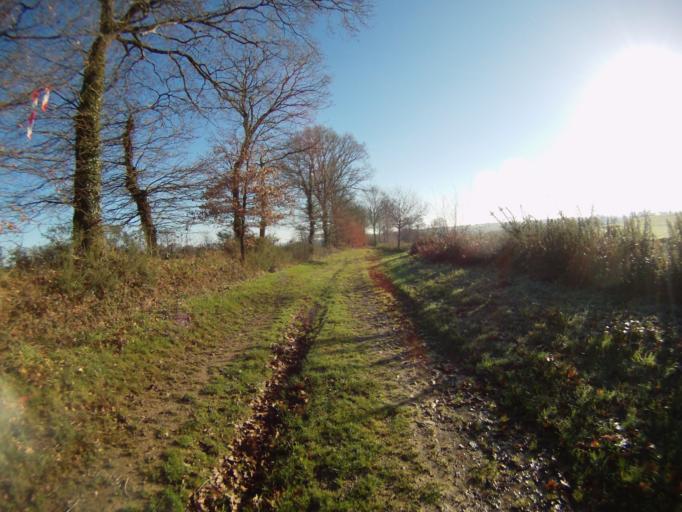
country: FR
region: Brittany
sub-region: Departement d'Ille-et-Vilaine
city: Chanteloup
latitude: 47.9367
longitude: -1.6239
